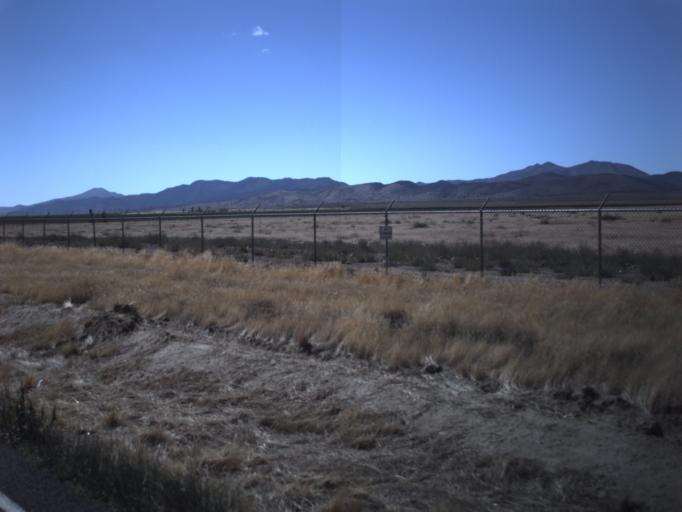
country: US
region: Utah
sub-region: Utah County
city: Genola
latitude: 40.0265
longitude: -111.9583
